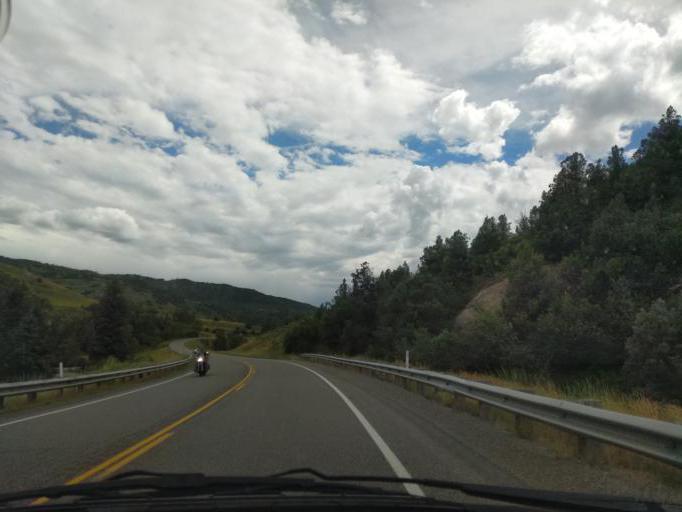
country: US
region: Colorado
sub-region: Delta County
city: Paonia
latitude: 39.0560
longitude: -107.3635
